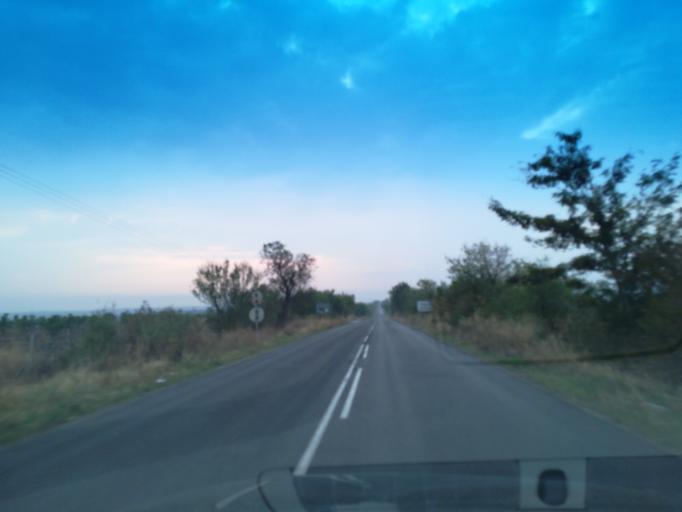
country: BG
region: Stara Zagora
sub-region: Obshtina Chirpan
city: Chirpan
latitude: 42.1956
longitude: 25.3094
